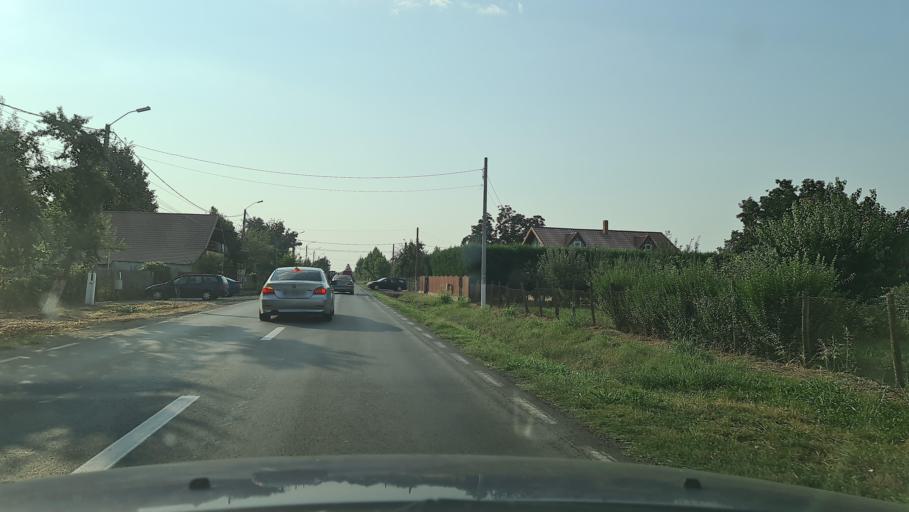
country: RO
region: Calarasi
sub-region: Comuna Dor Marunt
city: Dor Marunt
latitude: 44.4485
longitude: 26.9205
